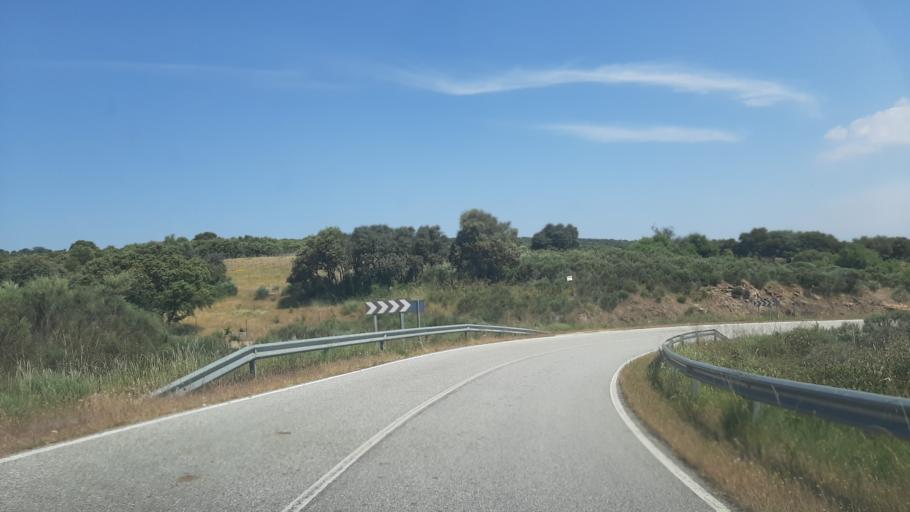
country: ES
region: Castille and Leon
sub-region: Provincia de Salamanca
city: Aldea del Obispo
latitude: 40.6501
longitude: -6.7806
